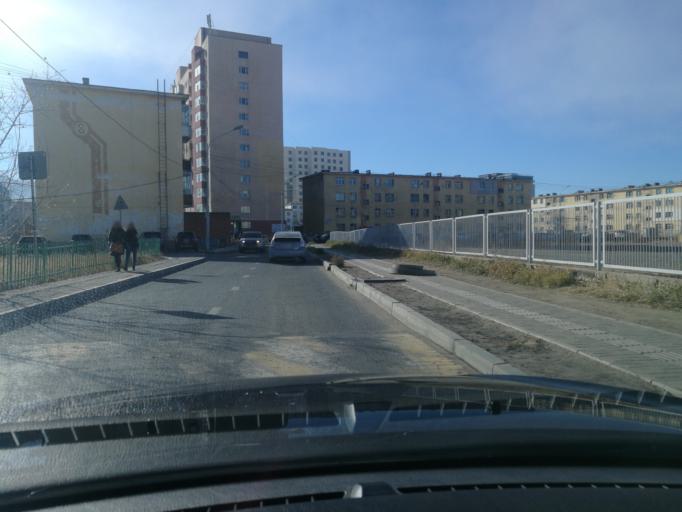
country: MN
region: Ulaanbaatar
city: Ulaanbaatar
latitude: 47.9019
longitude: 106.9073
